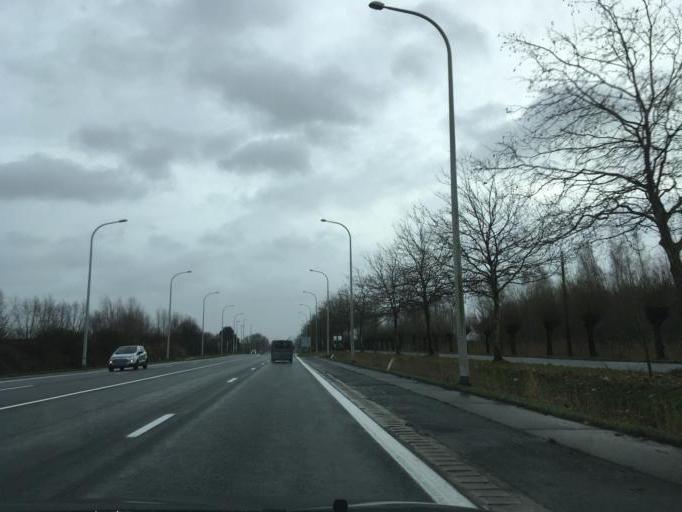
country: BE
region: Flanders
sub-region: Provincie West-Vlaanderen
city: Roeselare
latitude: 50.9236
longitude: 3.1352
